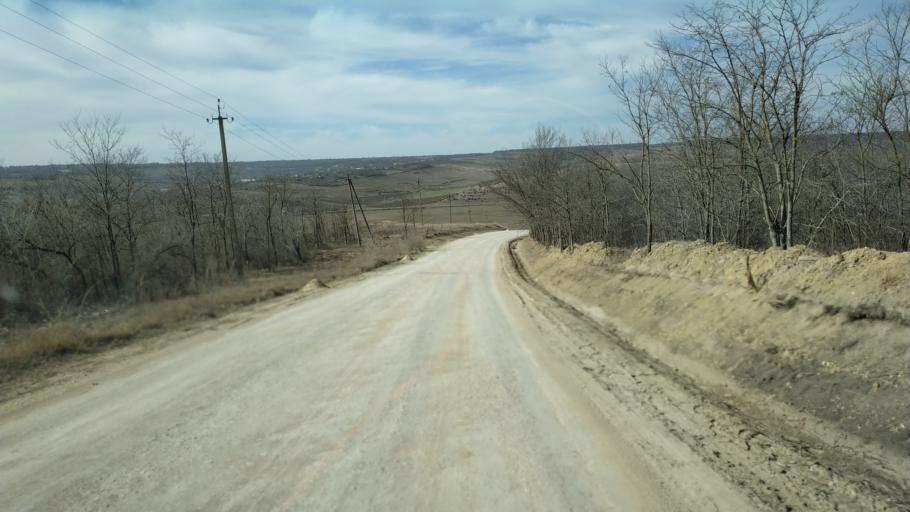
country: MD
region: Nisporeni
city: Nisporeni
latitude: 46.9738
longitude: 28.1911
